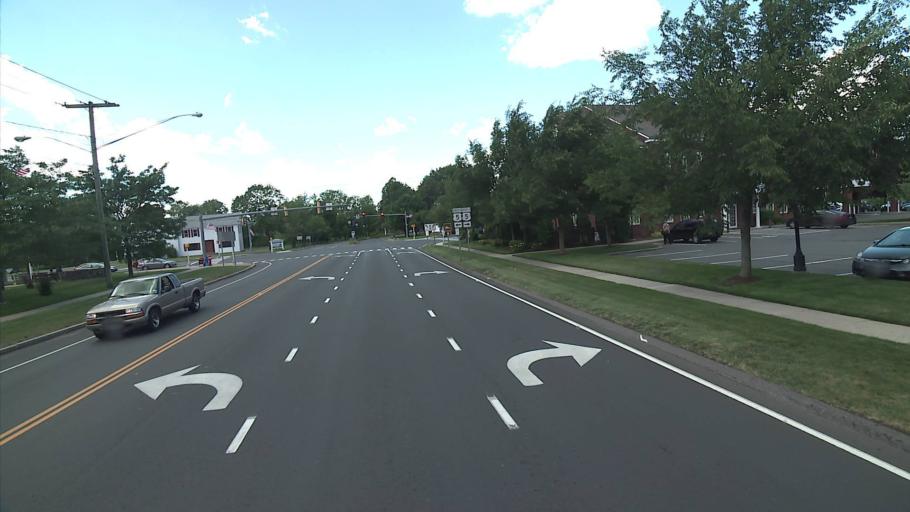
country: US
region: Connecticut
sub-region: Hartford County
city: Thompsonville
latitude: 41.9985
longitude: -72.5934
